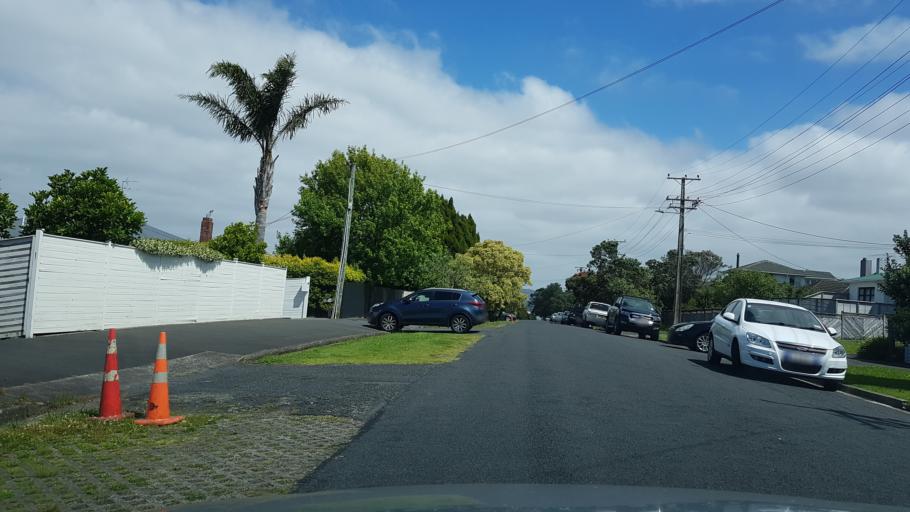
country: NZ
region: Auckland
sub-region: Auckland
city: North Shore
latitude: -36.8119
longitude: 174.7380
